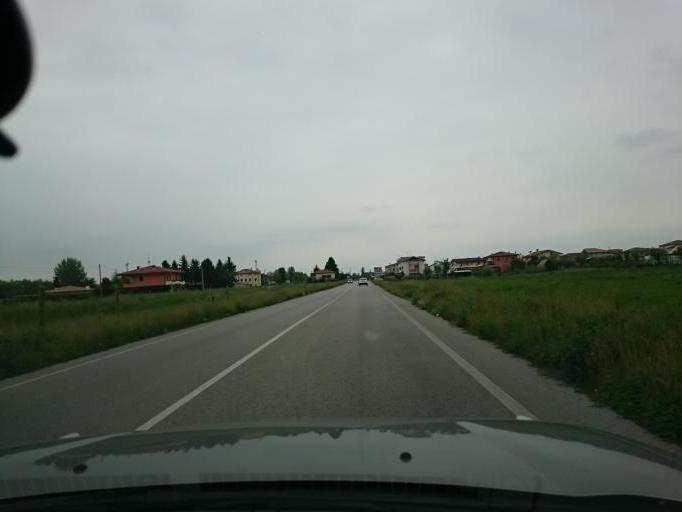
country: IT
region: Veneto
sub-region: Provincia di Padova
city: Terradura
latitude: 45.3219
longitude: 11.8053
